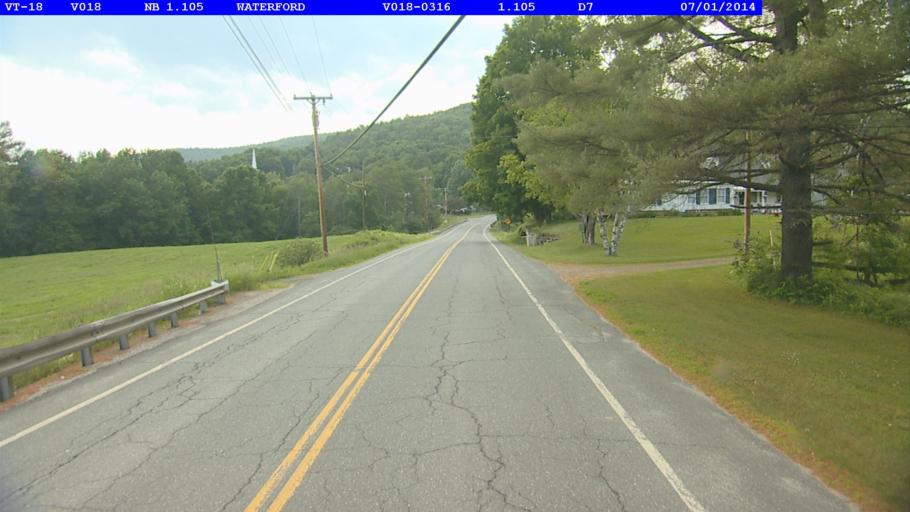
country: US
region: Vermont
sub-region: Caledonia County
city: Saint Johnsbury
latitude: 44.3537
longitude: -71.9044
